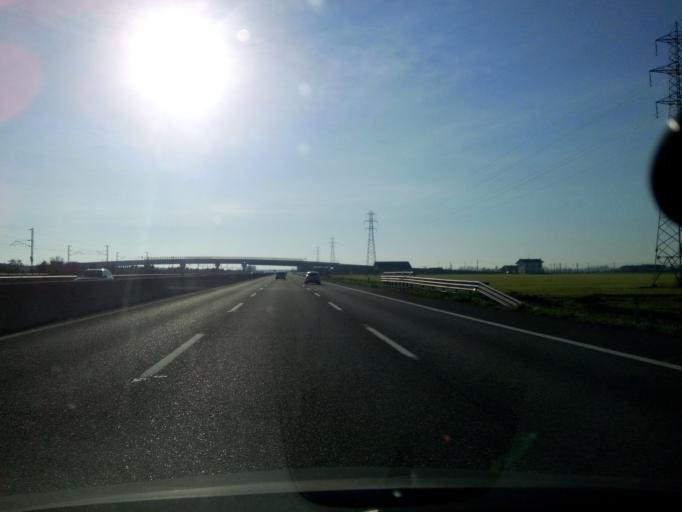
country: IT
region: Emilia-Romagna
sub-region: Provincia di Reggio Emilia
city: Prato
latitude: 44.7039
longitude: 10.7397
